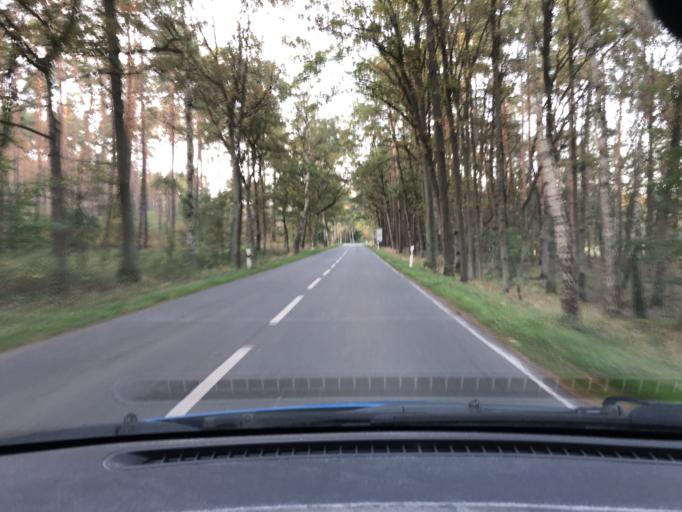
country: DE
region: Lower Saxony
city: Hitzacker
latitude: 53.1340
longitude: 11.0466
